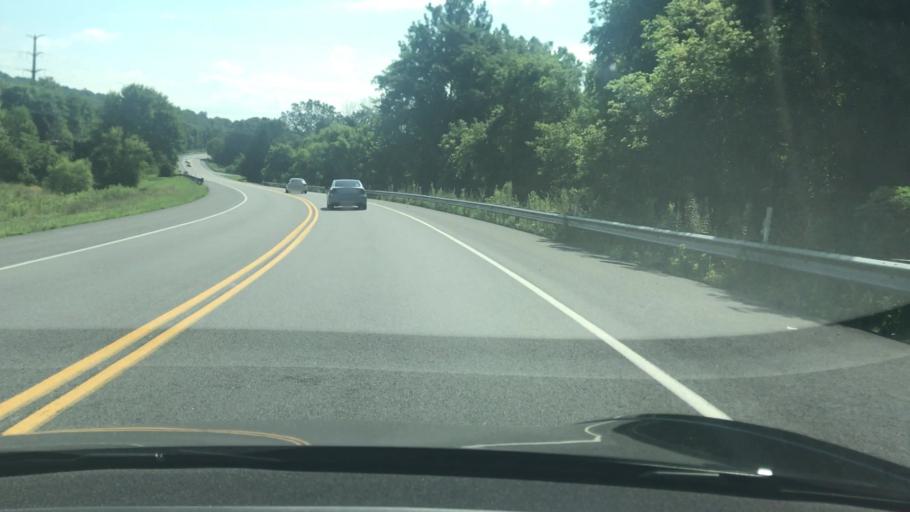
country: US
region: Pennsylvania
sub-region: York County
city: Valley Green
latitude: 40.1301
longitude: -76.8321
